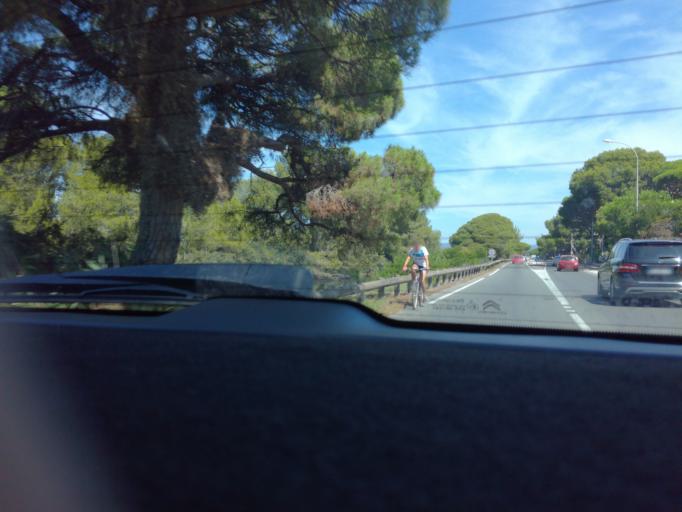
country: FR
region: Provence-Alpes-Cote d'Azur
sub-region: Departement du Var
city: Hyeres
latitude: 43.0742
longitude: 6.1485
